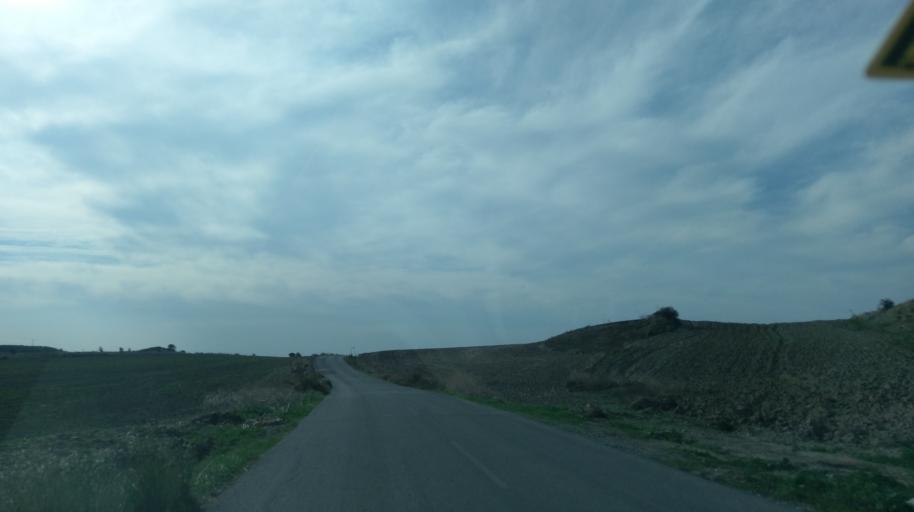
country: CY
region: Keryneia
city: Lapithos
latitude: 35.2797
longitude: 33.1892
